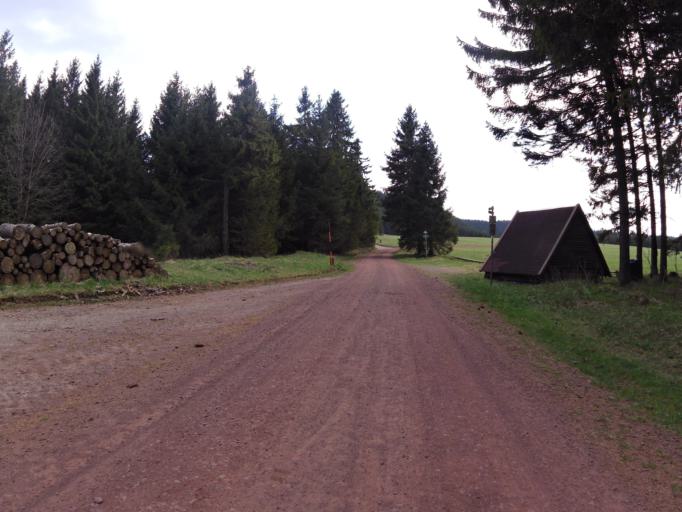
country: DE
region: Thuringia
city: Unterschonau
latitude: 50.7609
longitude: 10.5633
